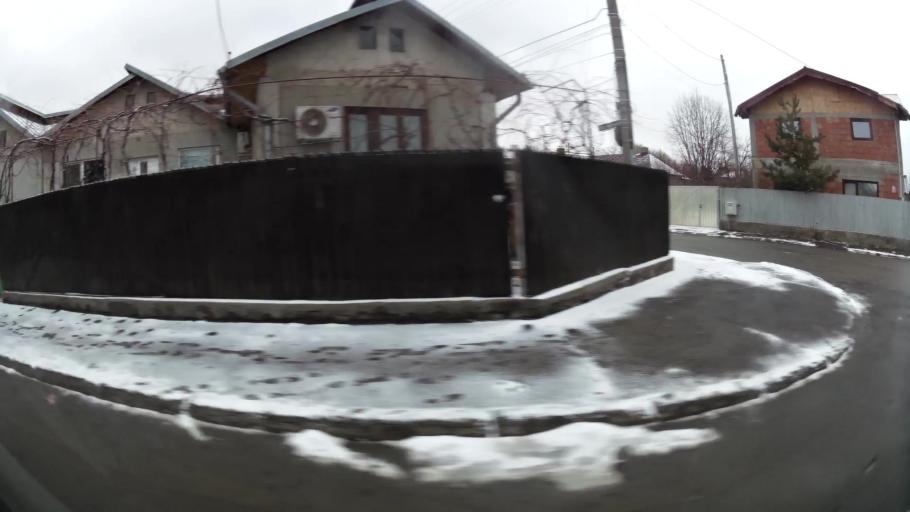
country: RO
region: Prahova
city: Ploiesti
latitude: 44.9324
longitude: 26.0496
